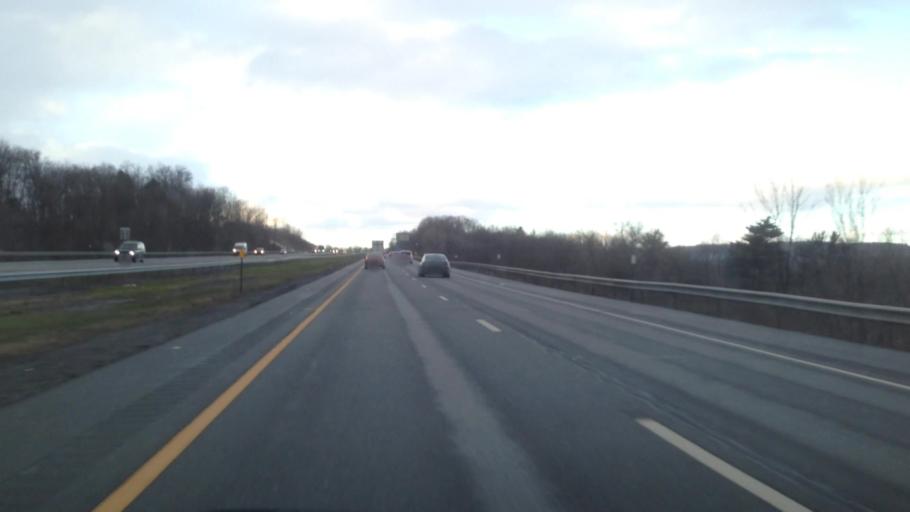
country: US
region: New York
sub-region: Herkimer County
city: Little Falls
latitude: 43.0111
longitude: -74.7910
